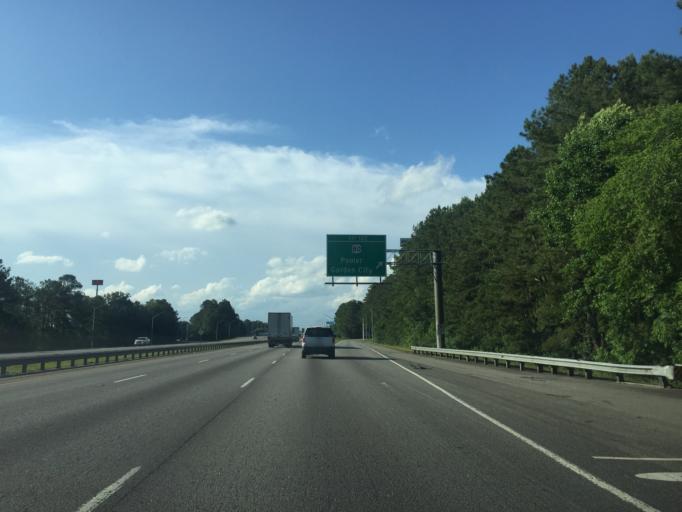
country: US
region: Georgia
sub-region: Chatham County
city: Pooler
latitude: 32.1064
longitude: -81.2372
